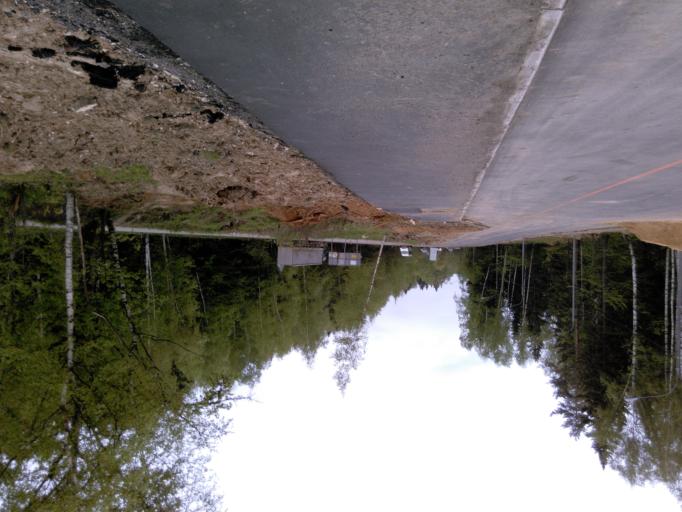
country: RU
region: Moskovskaya
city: Mendeleyevo
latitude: 56.0161
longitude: 37.2065
